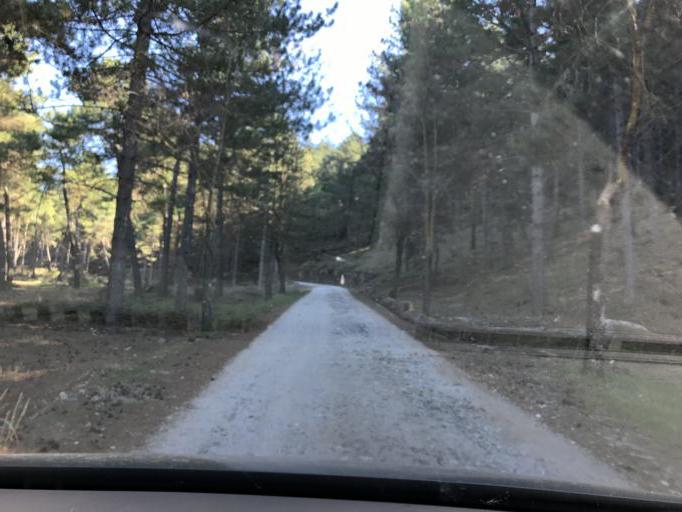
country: ES
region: Andalusia
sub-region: Provincia de Granada
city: Beas de Granada
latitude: 37.2548
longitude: -3.4706
